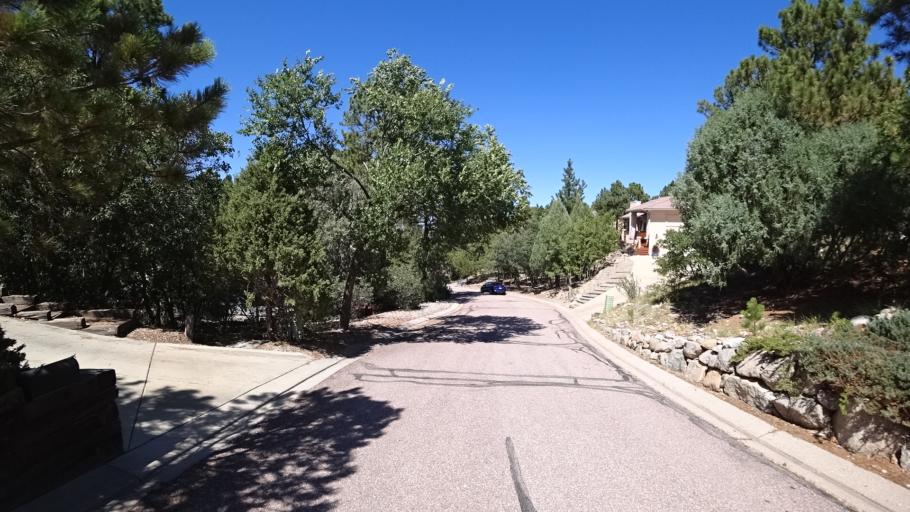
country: US
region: Colorado
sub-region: El Paso County
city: Colorado Springs
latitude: 38.9206
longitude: -104.8028
